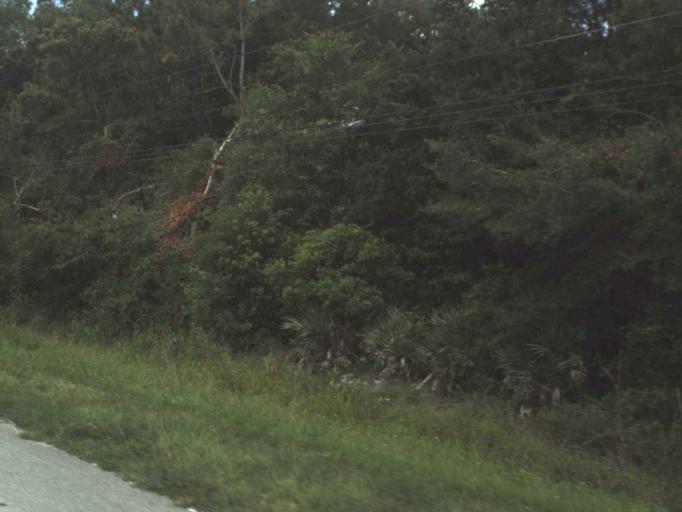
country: US
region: Florida
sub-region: Volusia County
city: Samsula-Spruce Creek
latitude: 28.9553
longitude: -81.0940
